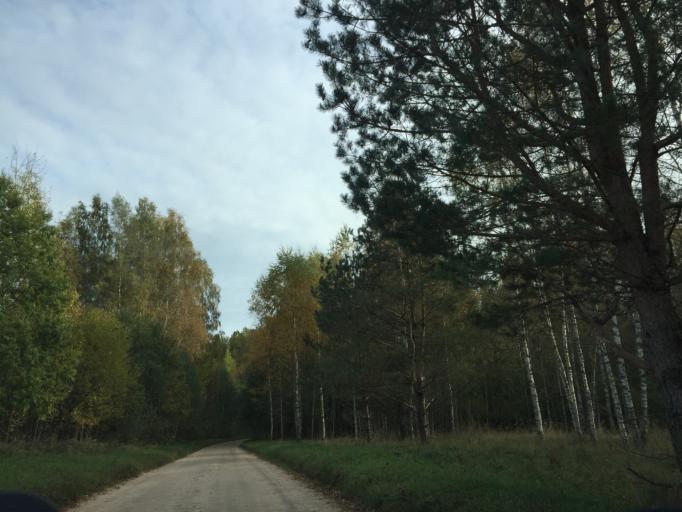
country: LV
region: Jaunpils
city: Jaunpils
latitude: 56.5703
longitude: 23.0274
